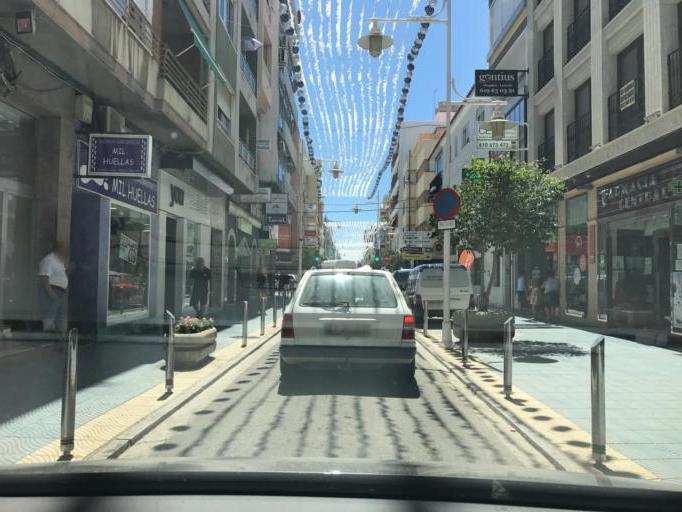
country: ES
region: Andalusia
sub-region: Provincia de Malaga
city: Velez-Malaga
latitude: 36.7418
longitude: -4.0949
